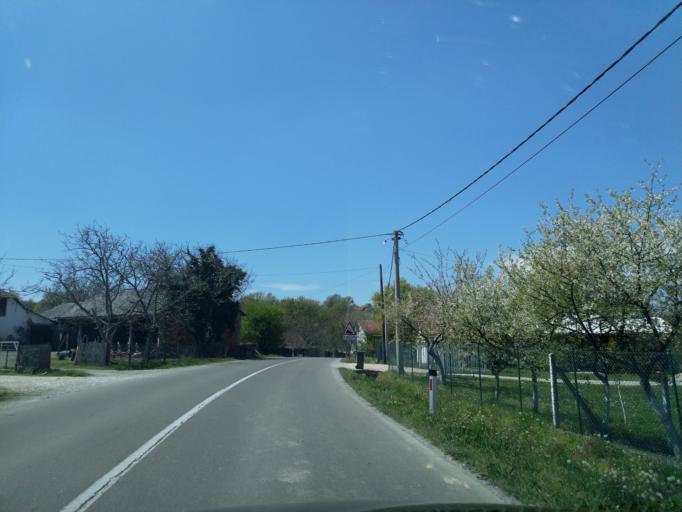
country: RS
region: Central Serbia
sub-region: Belgrade
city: Lazarevac
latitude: 44.3499
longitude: 20.3803
